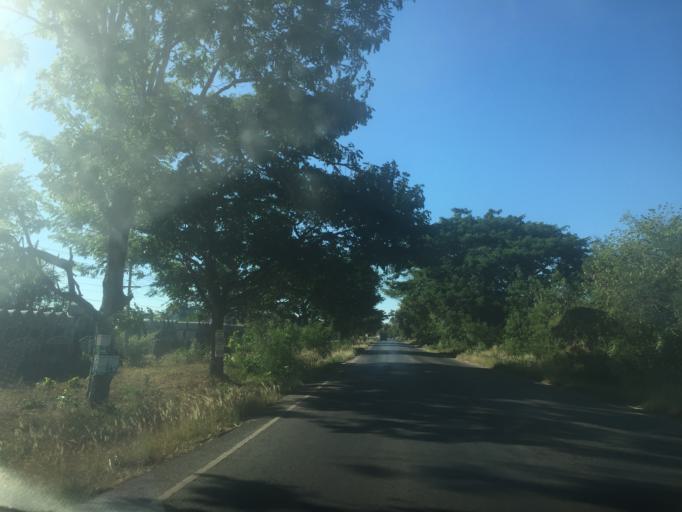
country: TH
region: Changwat Udon Thani
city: Si That
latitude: 16.9721
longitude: 103.2320
